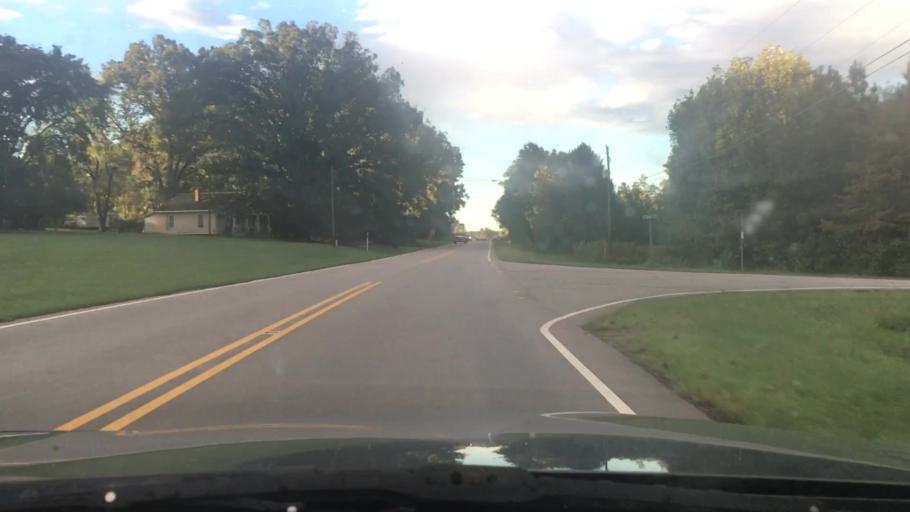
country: US
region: North Carolina
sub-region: Caswell County
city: Yanceyville
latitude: 36.4009
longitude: -79.3292
